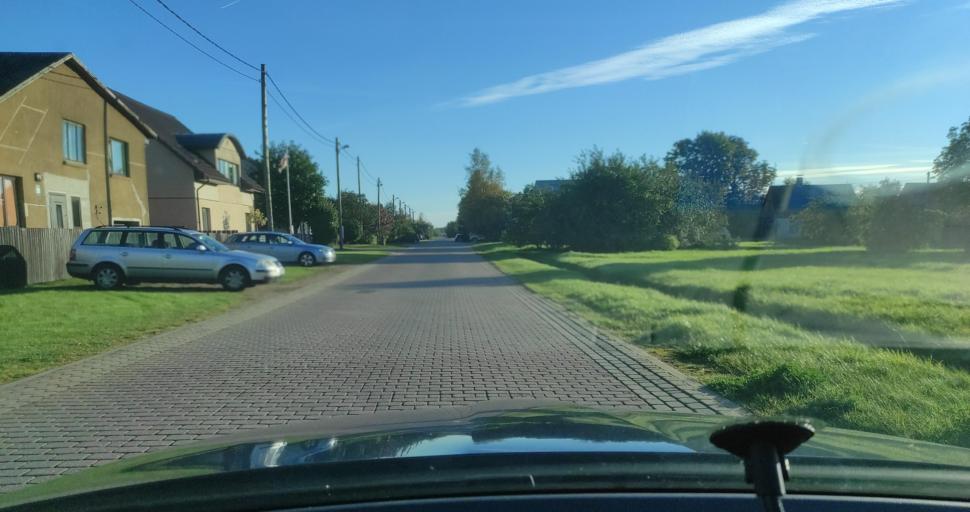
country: LV
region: Ventspils
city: Ventspils
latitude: 57.3725
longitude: 21.5768
